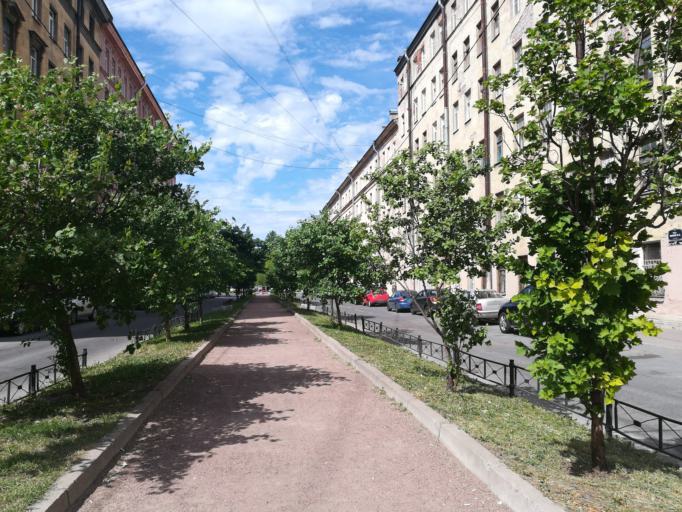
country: RU
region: St.-Petersburg
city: Vasyl'evsky Ostrov
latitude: 59.9467
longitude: 30.2611
